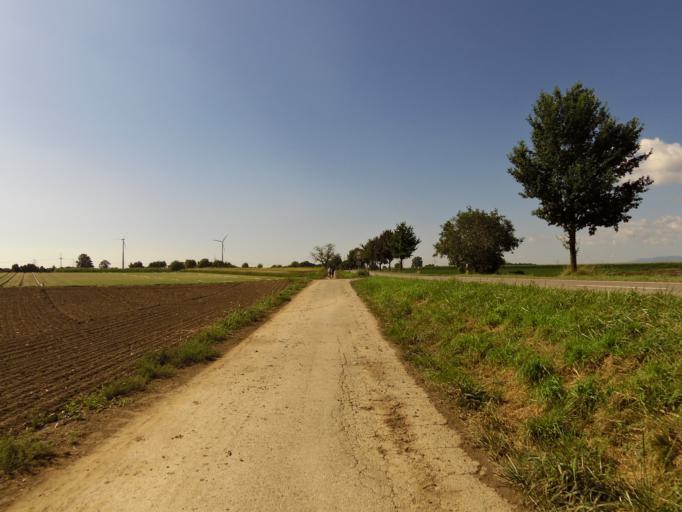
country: DE
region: Rheinland-Pfalz
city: Dannstadt-Schauernheim
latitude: 49.4196
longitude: 8.3176
